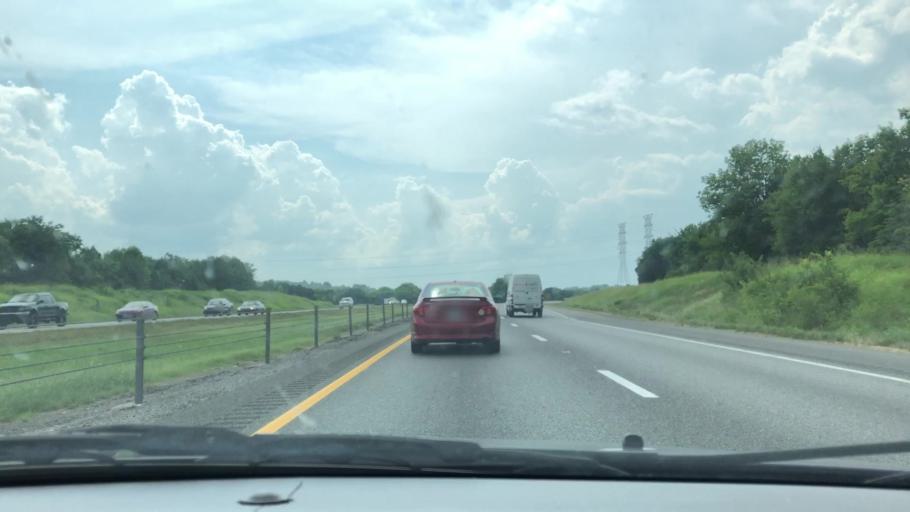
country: US
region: Tennessee
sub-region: Wilson County
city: Lebanon
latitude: 36.1836
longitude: -86.3412
